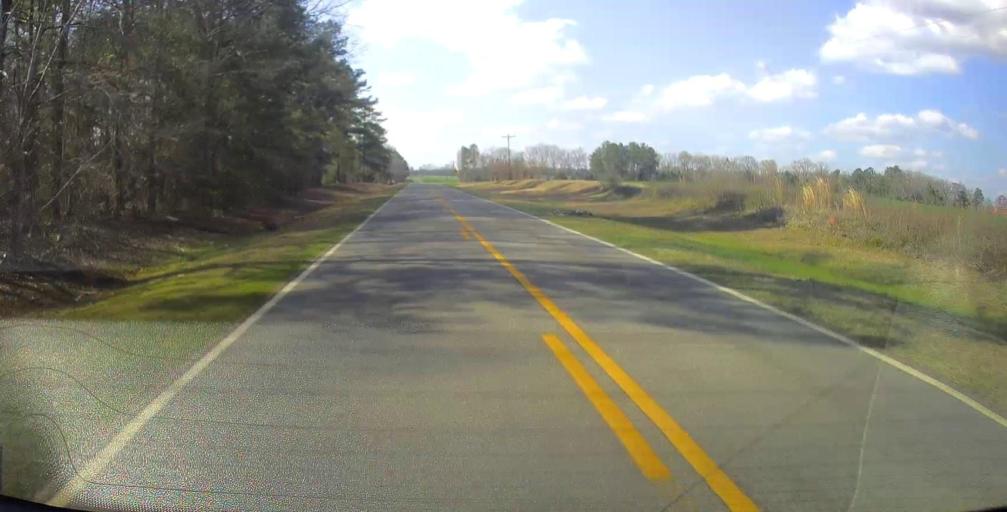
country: US
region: Georgia
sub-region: Wilkinson County
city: Irwinton
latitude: 32.6288
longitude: -83.0974
